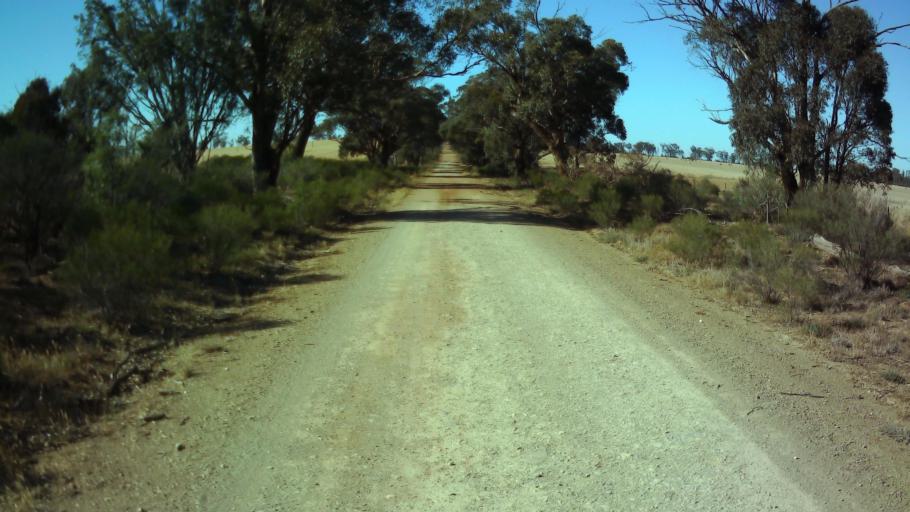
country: AU
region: New South Wales
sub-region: Weddin
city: Grenfell
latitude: -33.8919
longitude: 147.8803
